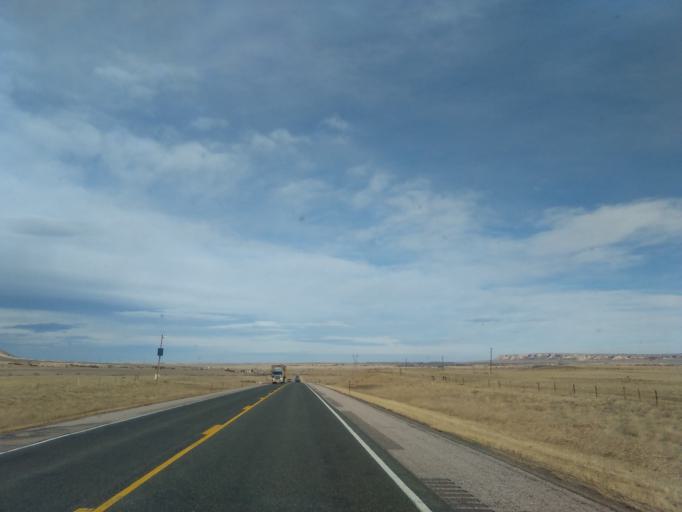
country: US
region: Wyoming
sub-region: Goshen County
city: Torrington
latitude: 41.6239
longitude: -104.2479
